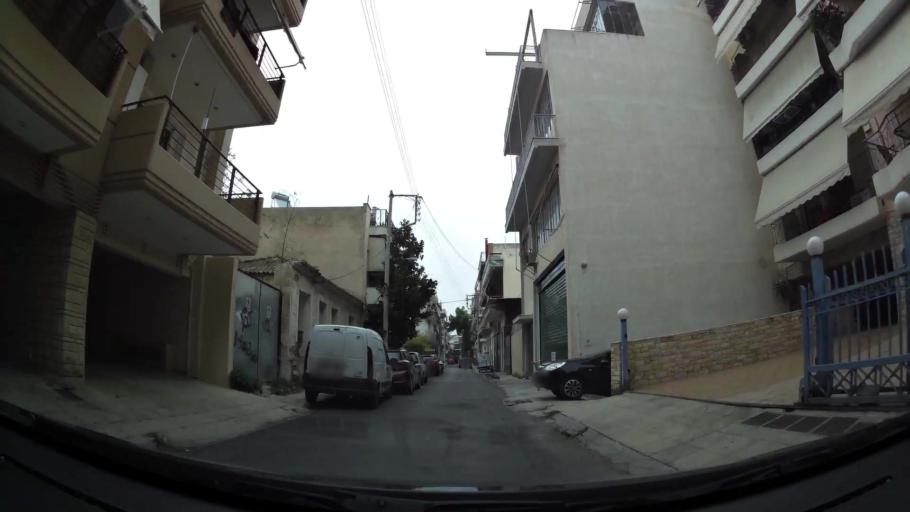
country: GR
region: Attica
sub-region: Nomos Piraios
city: Agios Ioannis Rentis
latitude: 37.9568
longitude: 23.6577
